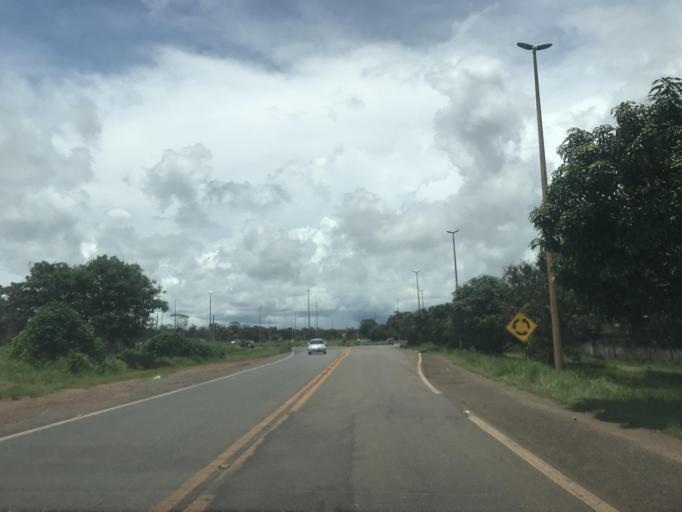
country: BR
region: Federal District
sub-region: Brasilia
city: Brasilia
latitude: -15.6901
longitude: -47.8328
